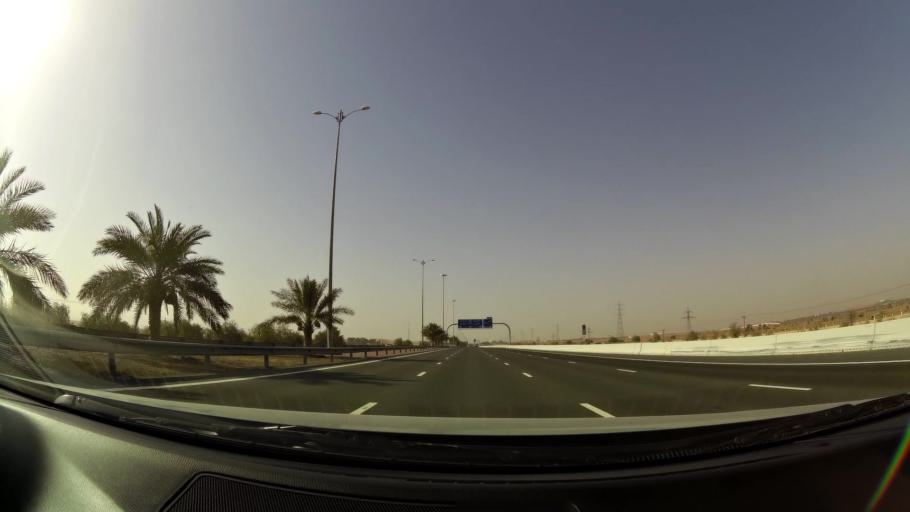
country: OM
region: Al Buraimi
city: Al Buraymi
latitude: 24.5039
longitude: 55.7672
